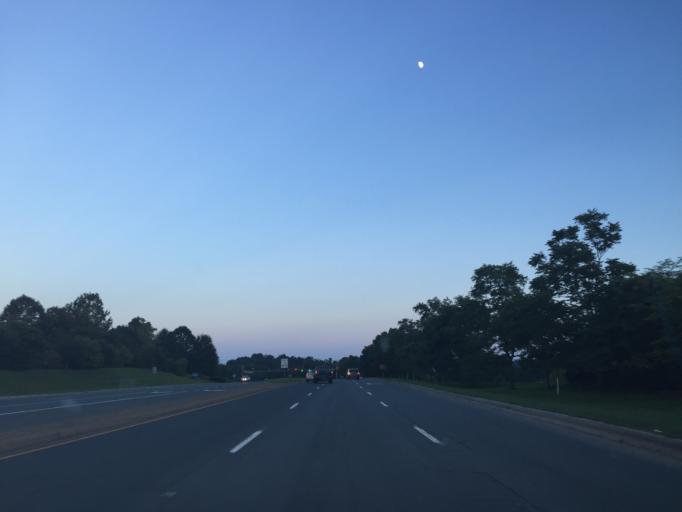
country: US
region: Virginia
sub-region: City of Charlottesville
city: Charlottesville
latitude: 38.0284
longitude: -78.4409
